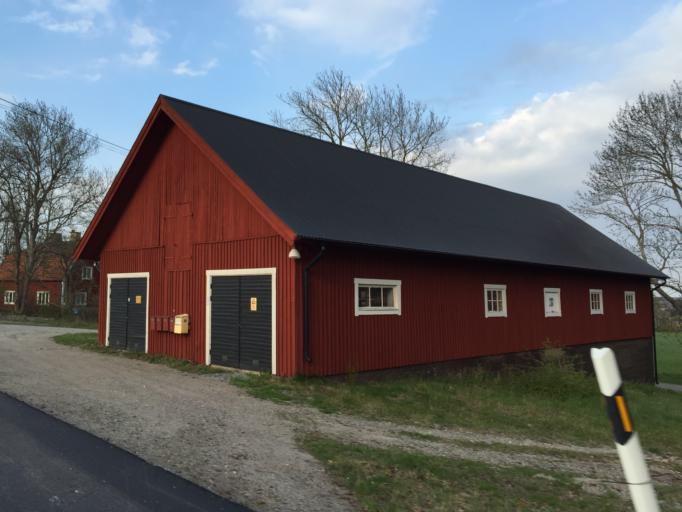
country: SE
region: Soedermanland
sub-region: Trosa Kommun
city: Vagnharad
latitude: 59.0352
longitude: 17.5991
